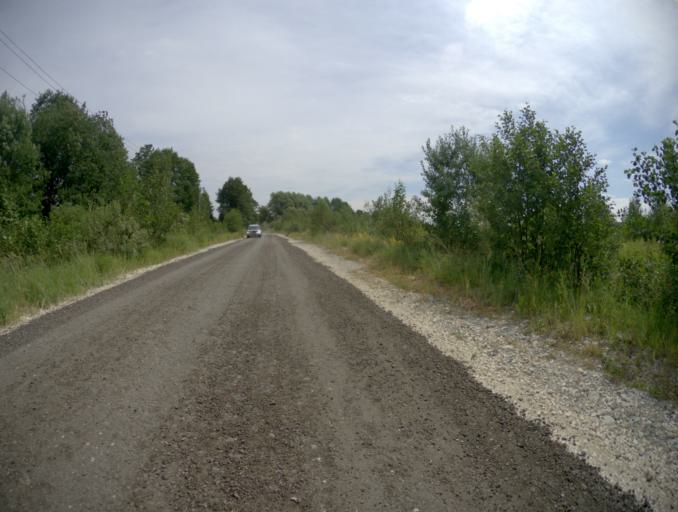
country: RU
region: Vladimir
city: Raduzhnyy
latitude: 56.0280
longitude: 40.2938
